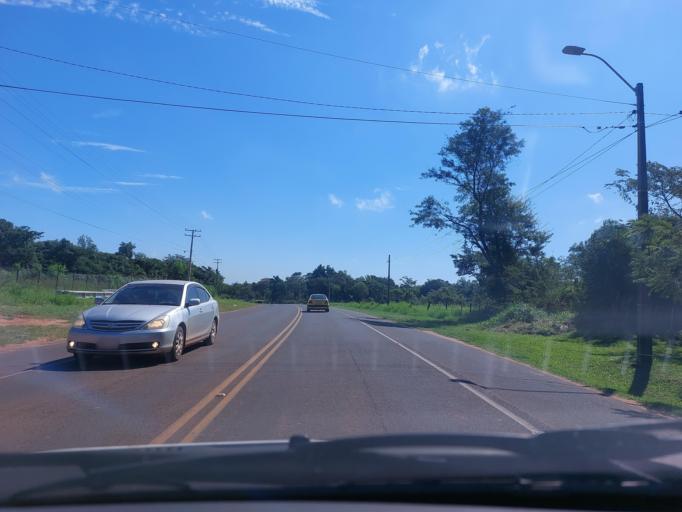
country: PY
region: San Pedro
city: Guayaybi
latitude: -24.6611
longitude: -56.4578
